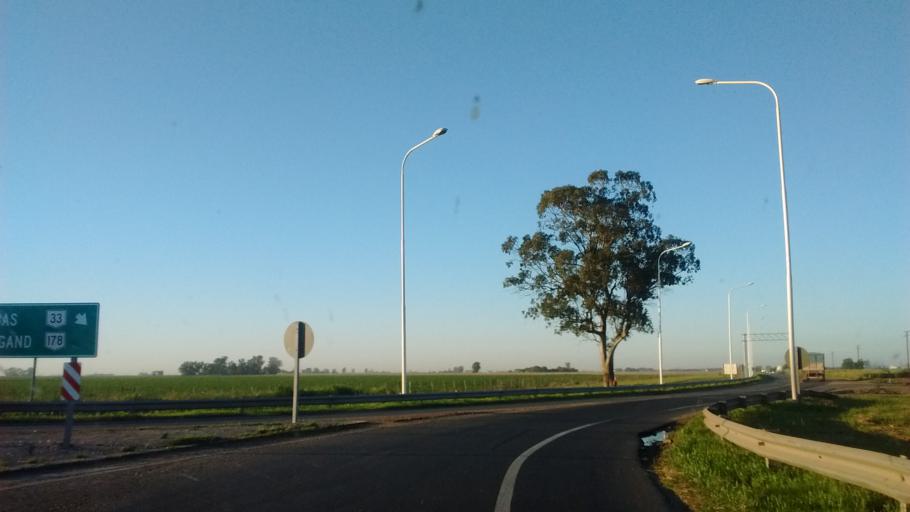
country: AR
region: Santa Fe
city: Casilda
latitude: -33.1999
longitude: -61.3232
